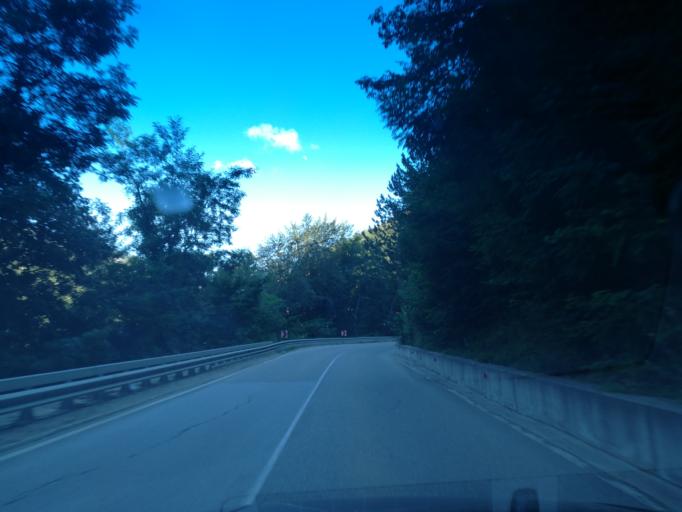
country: BG
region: Smolyan
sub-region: Obshtina Chepelare
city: Chepelare
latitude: 41.8236
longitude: 24.6916
